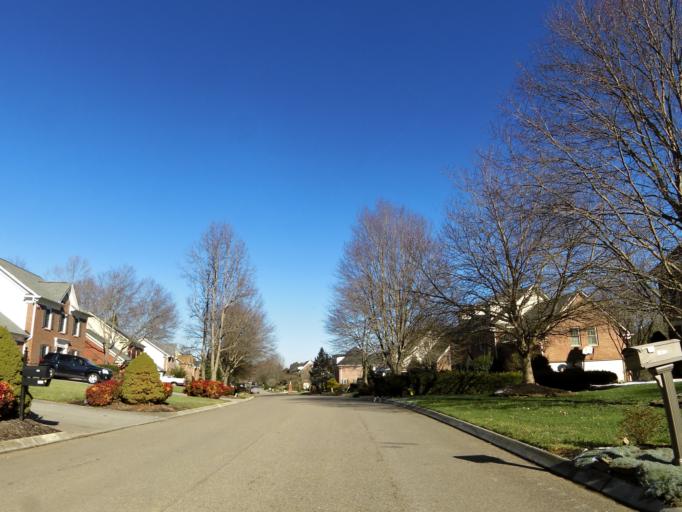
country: US
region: Tennessee
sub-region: Blount County
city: Louisville
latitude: 35.9183
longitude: -84.0264
